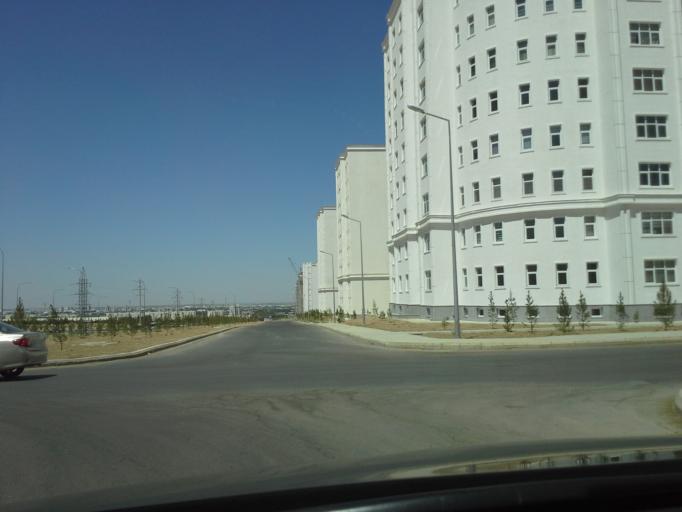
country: TM
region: Ahal
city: Ashgabat
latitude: 37.8926
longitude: 58.4061
